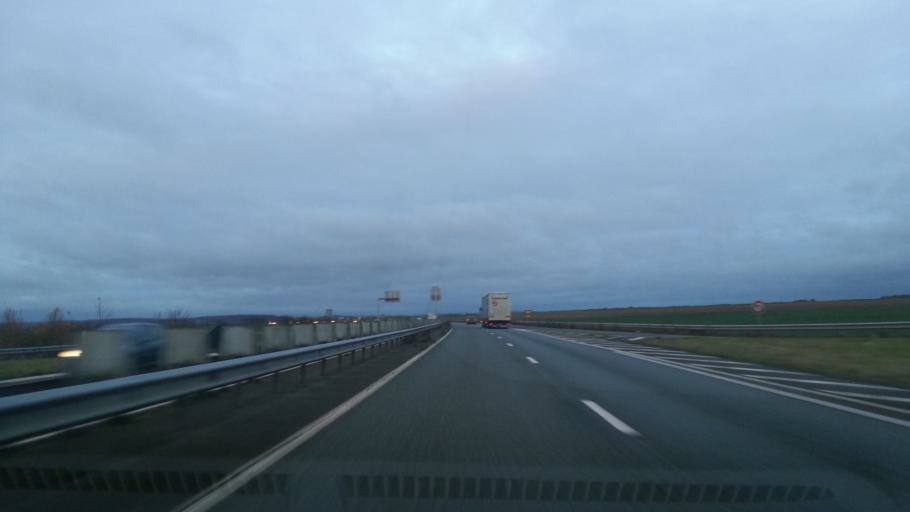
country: FR
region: Picardie
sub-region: Departement de l'Oise
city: Bresles
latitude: 49.4147
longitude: 2.3018
